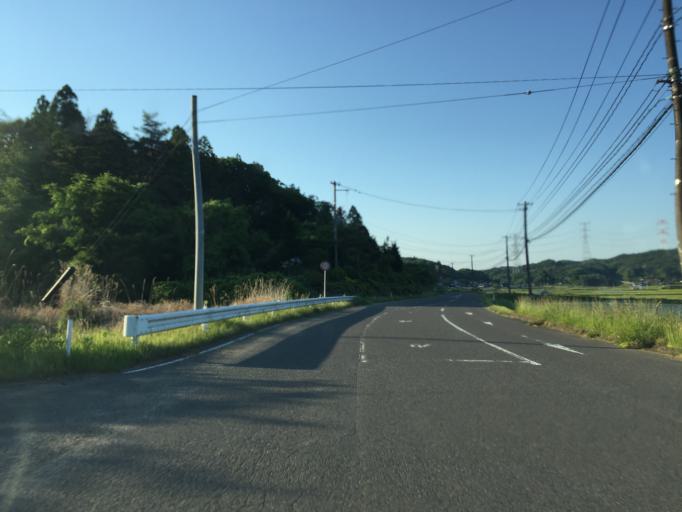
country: JP
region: Fukushima
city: Ishikawa
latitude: 37.0579
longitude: 140.4202
